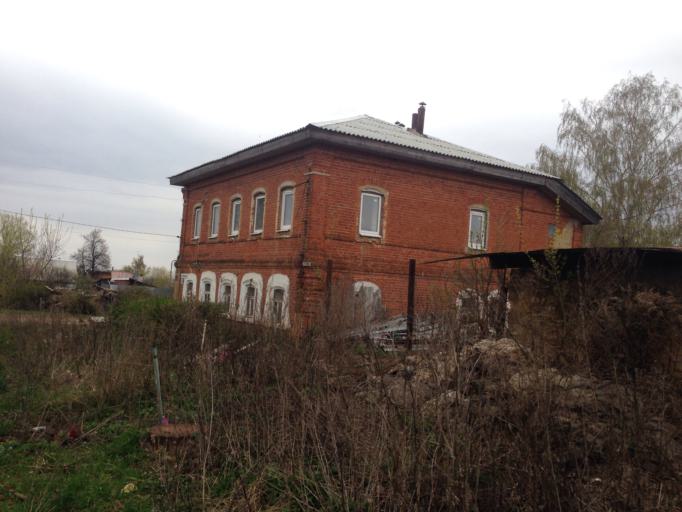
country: RU
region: Tula
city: Krapivna
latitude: 53.9406
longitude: 37.1511
